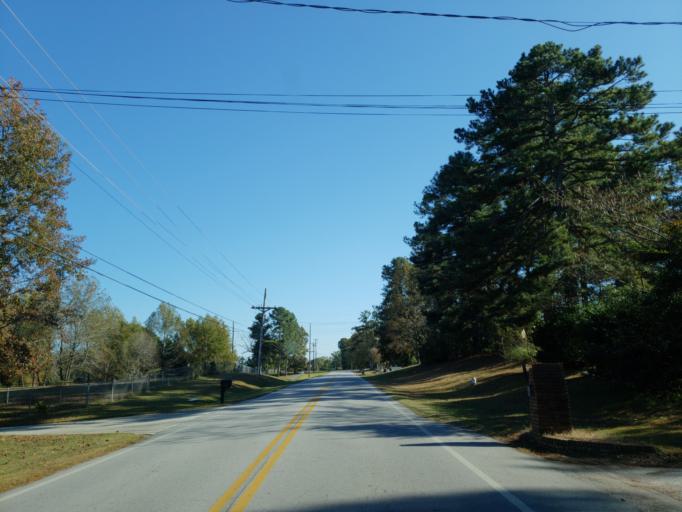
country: US
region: Georgia
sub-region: Gwinnett County
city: Lawrenceville
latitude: 33.9929
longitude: -83.9753
